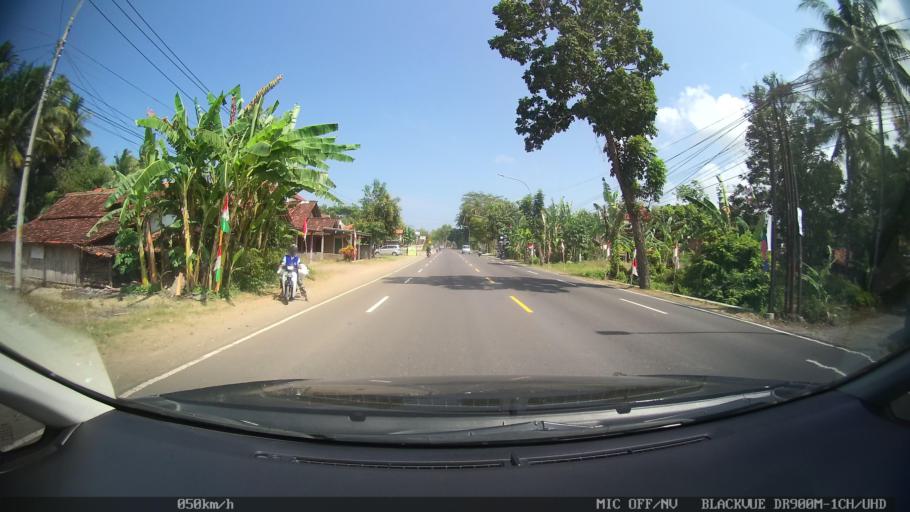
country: ID
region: Daerah Istimewa Yogyakarta
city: Srandakan
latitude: -7.8876
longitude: 110.0895
